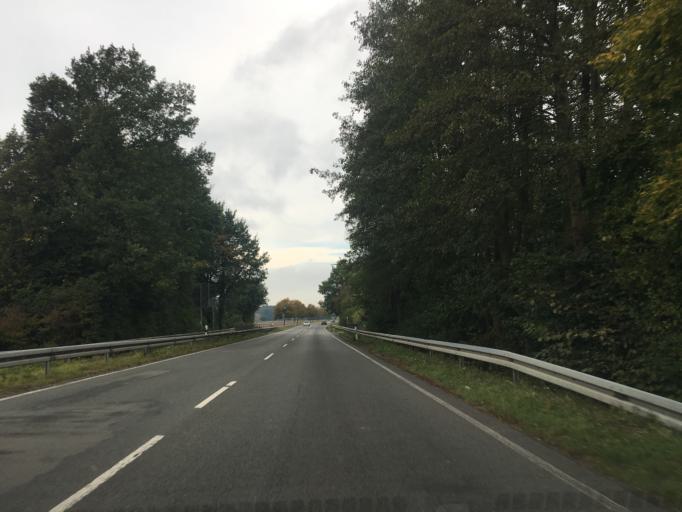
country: DE
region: North Rhine-Westphalia
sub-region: Regierungsbezirk Munster
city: Schoppingen
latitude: 52.0959
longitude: 7.2204
